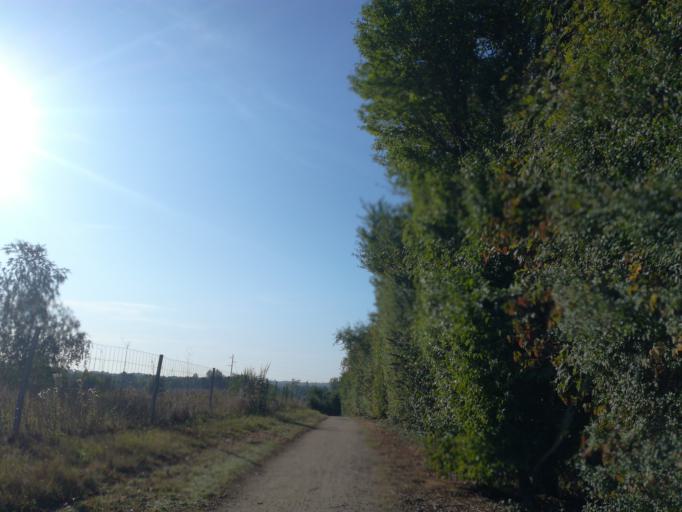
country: FR
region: Brittany
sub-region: Departement d'Ille-et-Vilaine
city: Fouillard
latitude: 48.1446
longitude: -1.5901
